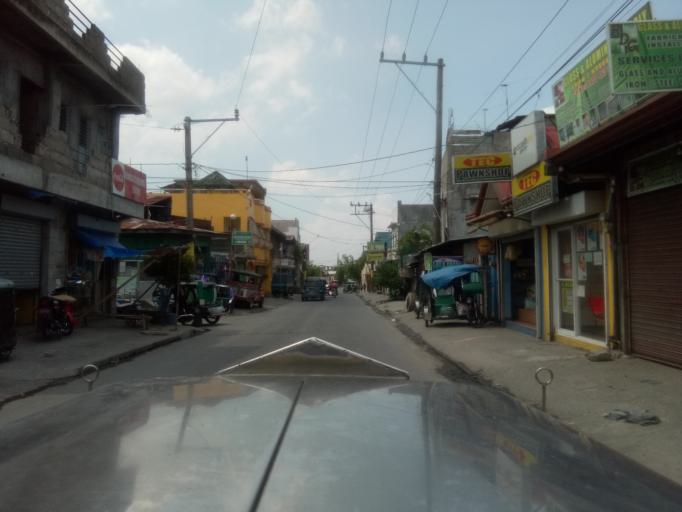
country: PH
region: Calabarzon
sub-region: Province of Cavite
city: Bulihan
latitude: 14.3141
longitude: 120.9764
